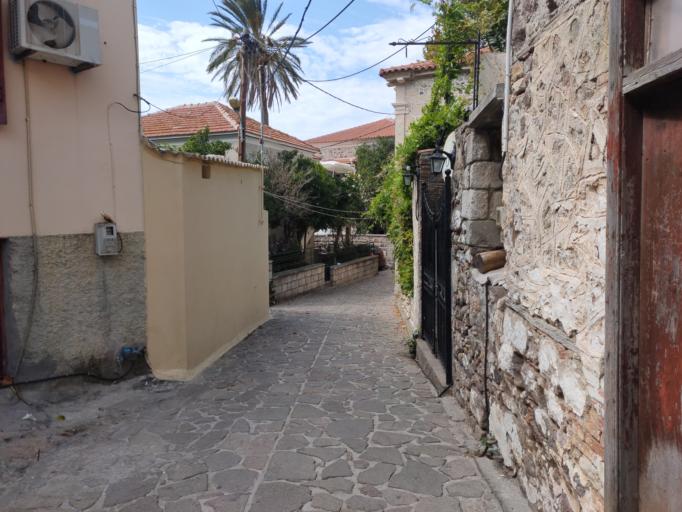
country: GR
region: North Aegean
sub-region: Nomos Lesvou
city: Petra
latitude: 39.3272
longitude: 26.1761
